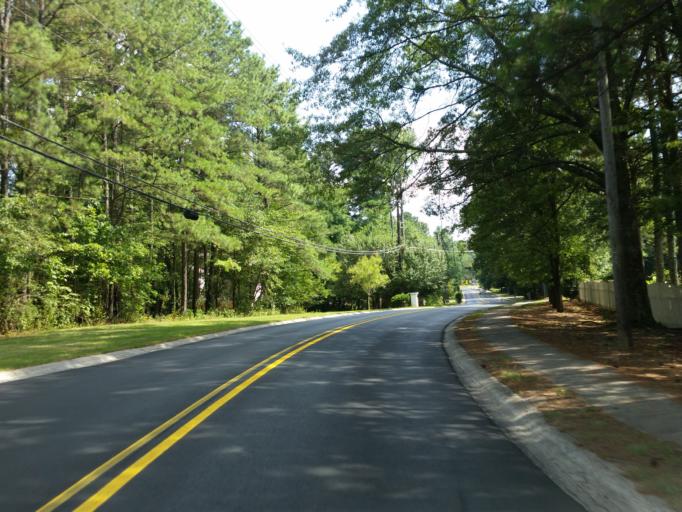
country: US
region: Georgia
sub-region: Cobb County
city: Marietta
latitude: 34.0025
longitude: -84.4637
